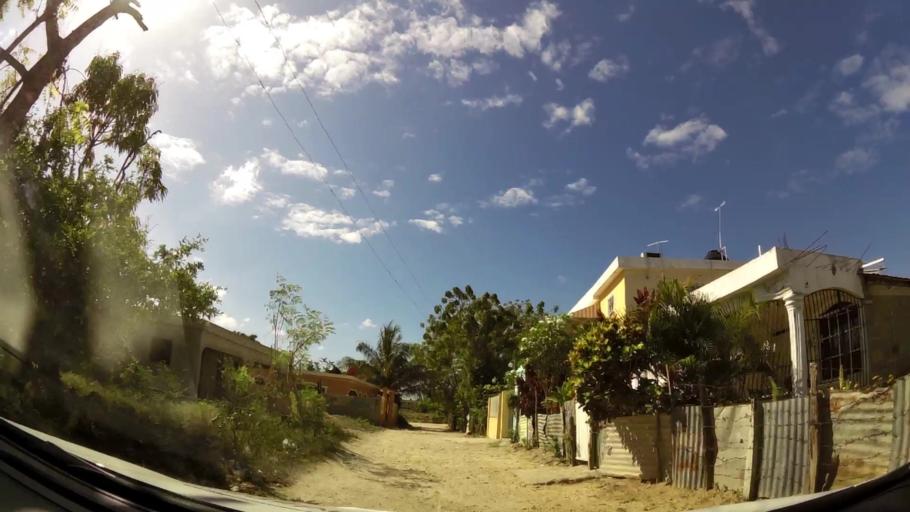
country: DO
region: Santo Domingo
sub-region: Santo Domingo
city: Boca Chica
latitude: 18.4622
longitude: -69.6100
